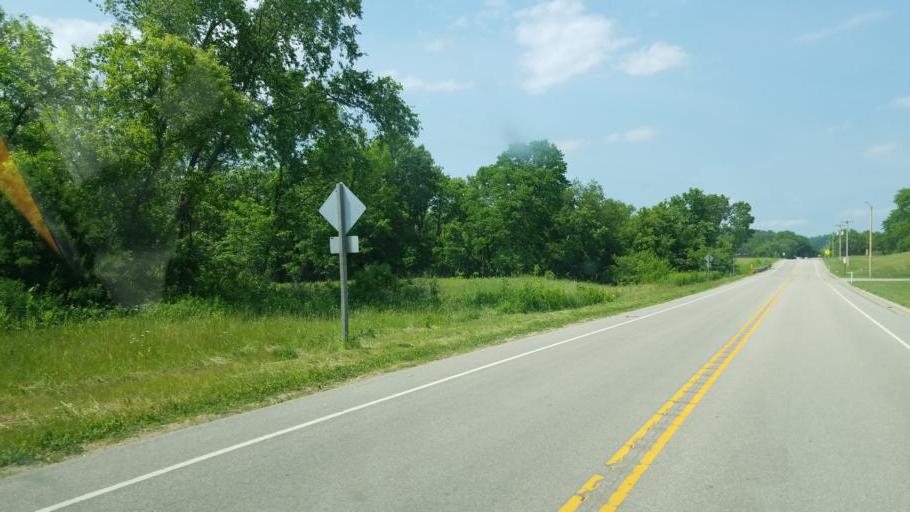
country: US
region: Wisconsin
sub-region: Vernon County
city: Viroqua
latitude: 43.4917
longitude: -90.6798
